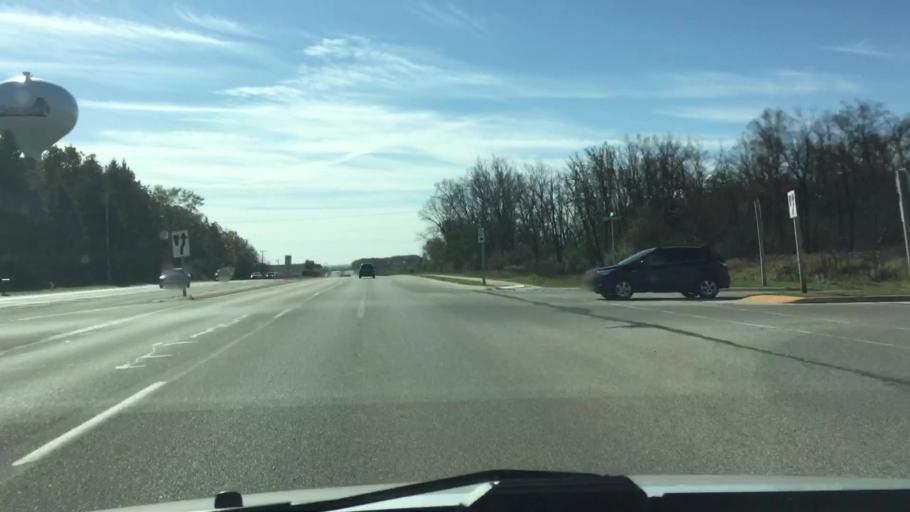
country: US
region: Wisconsin
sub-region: Waukesha County
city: Sussex
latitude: 43.1209
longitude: -88.2446
